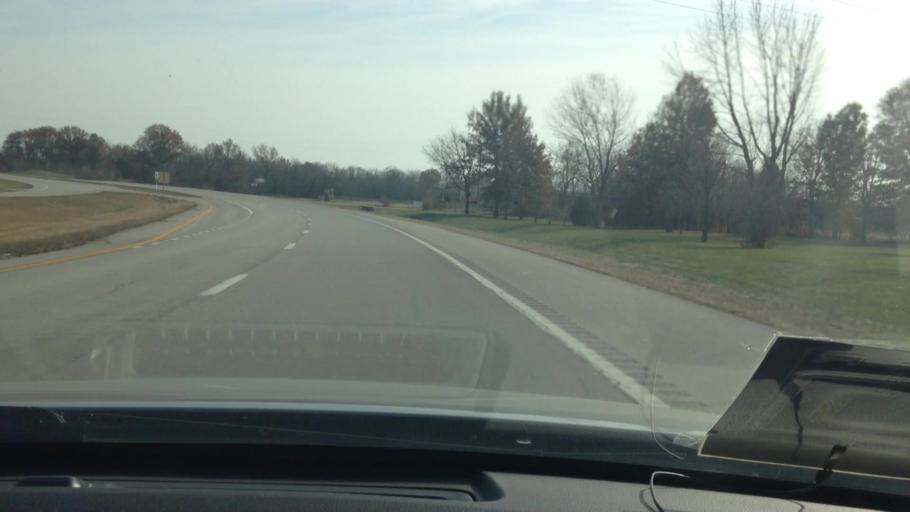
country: US
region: Missouri
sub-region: Cass County
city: Harrisonville
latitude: 38.6105
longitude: -94.3221
